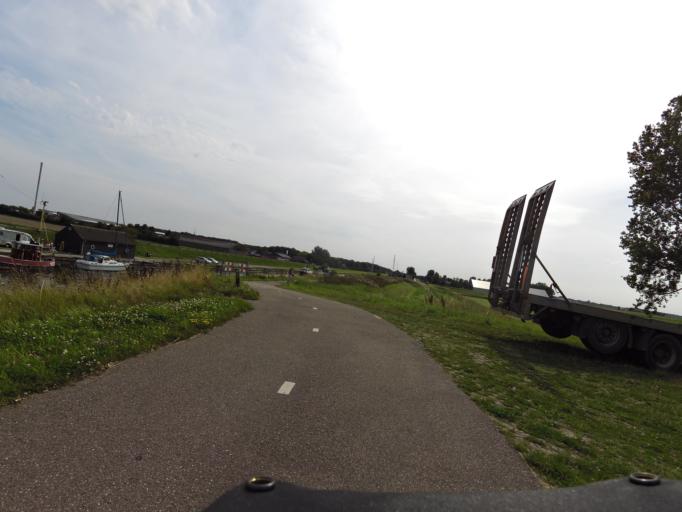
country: NL
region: South Holland
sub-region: Gemeente Goeree-Overflakkee
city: Middelharnis
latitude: 51.7714
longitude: 4.1851
